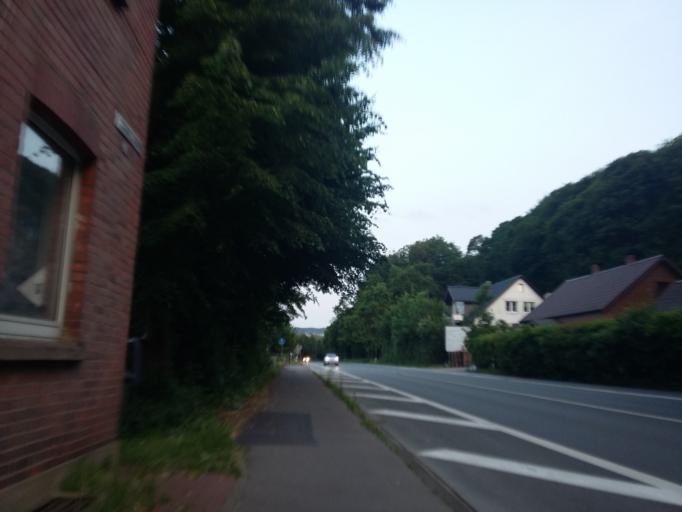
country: DE
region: North Rhine-Westphalia
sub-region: Regierungsbezirk Detmold
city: Vlotho
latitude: 52.1885
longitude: 8.8545
